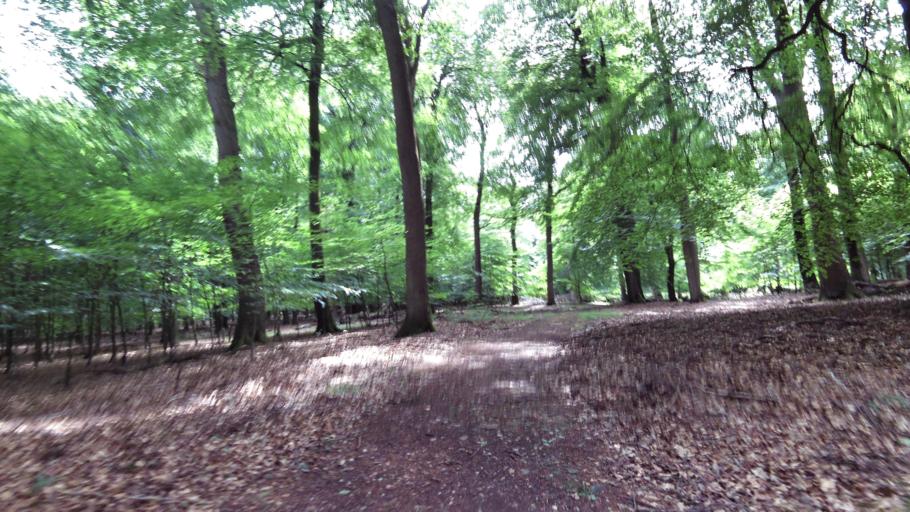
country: NL
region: Gelderland
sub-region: Gemeente Apeldoorn
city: Apeldoorn
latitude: 52.2306
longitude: 5.8895
